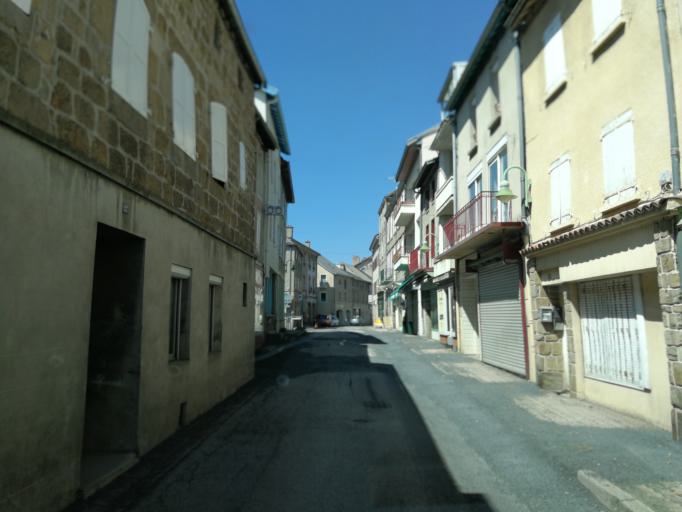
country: FR
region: Rhone-Alpes
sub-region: Departement de l'Ardeche
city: Saint-Agreve
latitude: 45.0094
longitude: 4.3973
